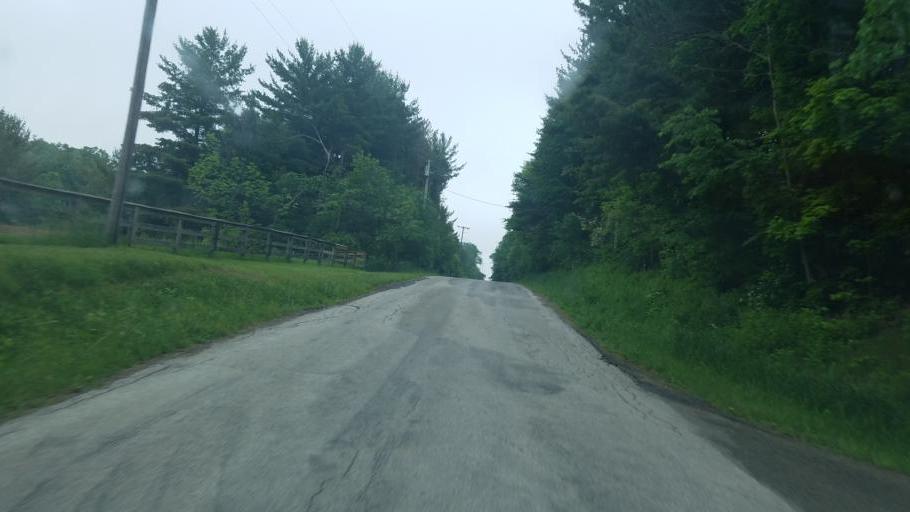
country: US
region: Ohio
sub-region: Sandusky County
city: Bellville
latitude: 40.6598
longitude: -82.4726
